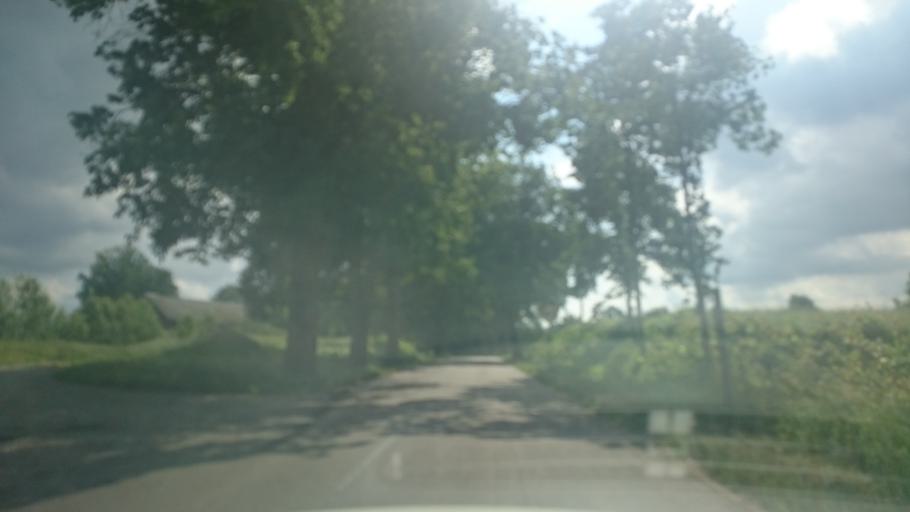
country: PL
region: Pomeranian Voivodeship
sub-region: Powiat starogardzki
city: Zblewo
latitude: 53.9674
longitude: 18.2607
